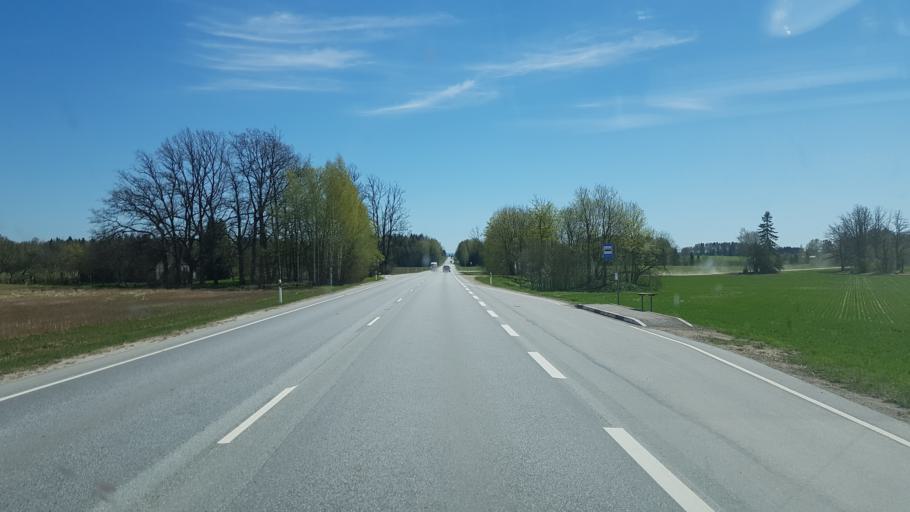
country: EE
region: Vorumaa
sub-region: Voru linn
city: Voru
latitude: 57.9052
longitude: 26.8325
